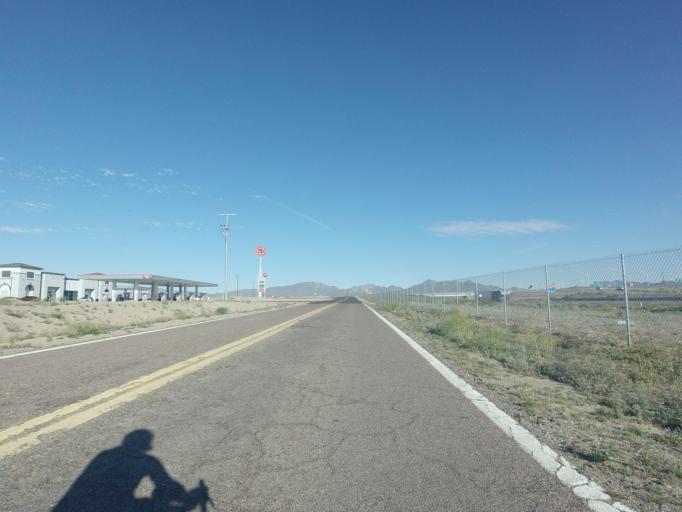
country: US
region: Arizona
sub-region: La Paz County
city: Ehrenberg
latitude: 33.6034
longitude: -114.5222
